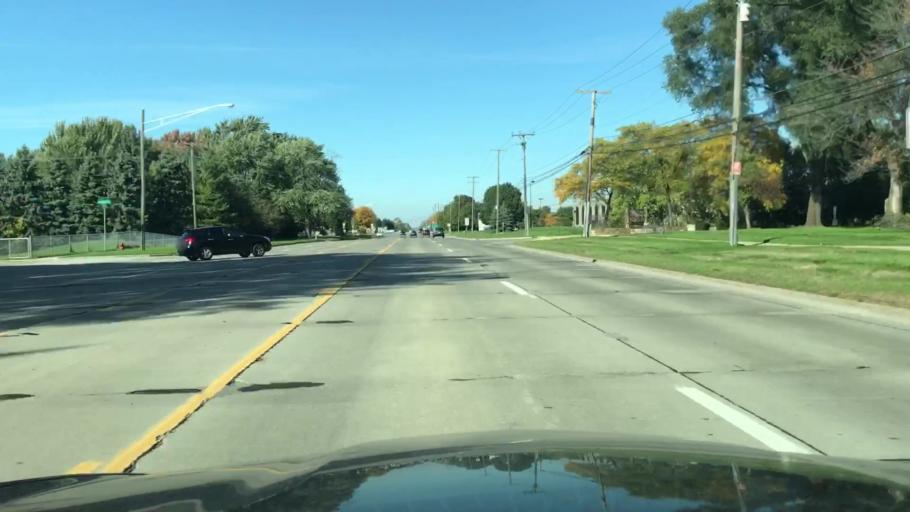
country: US
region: Michigan
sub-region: Macomb County
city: Sterling Heights
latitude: 42.5593
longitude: -83.0885
